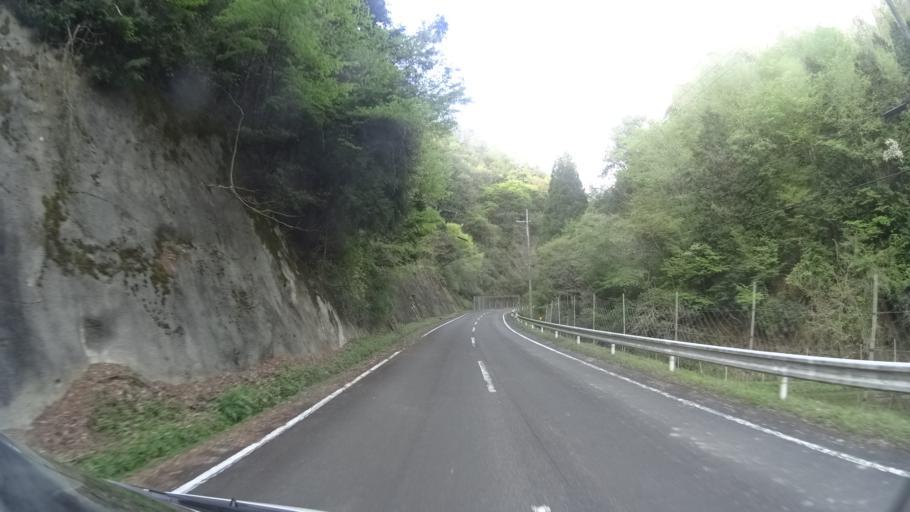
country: JP
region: Kyoto
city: Ayabe
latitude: 35.2521
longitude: 135.3098
